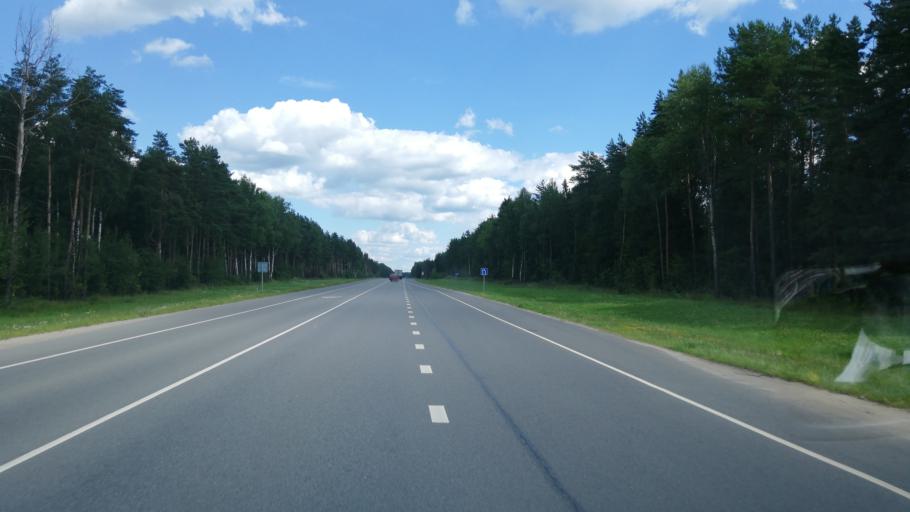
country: RU
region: Jaroslavl
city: Levashevo
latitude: 57.6397
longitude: 40.4673
